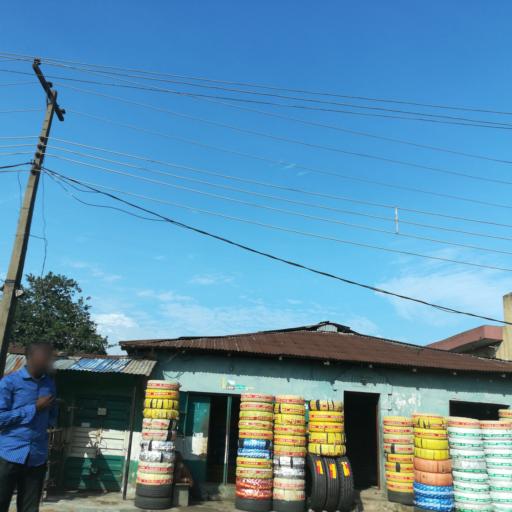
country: NG
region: Lagos
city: Agege
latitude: 6.6096
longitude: 3.3299
